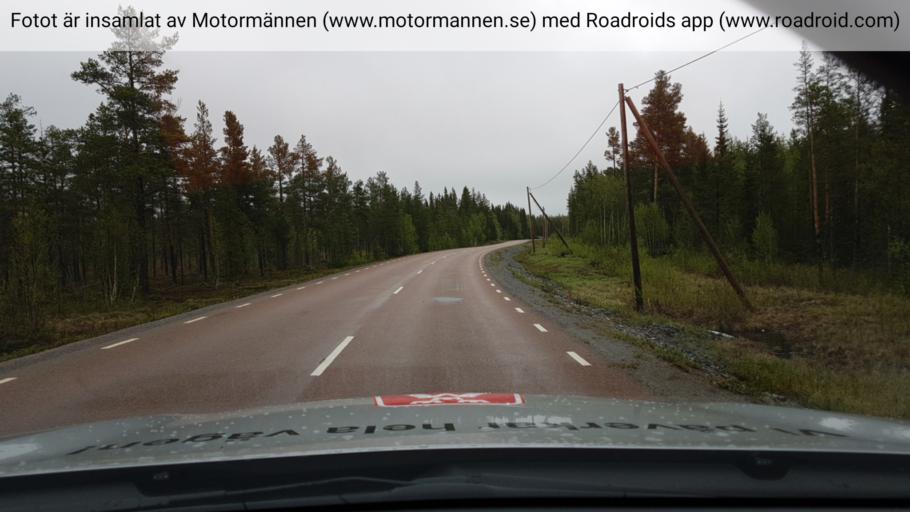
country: SE
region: Jaemtland
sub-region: Krokoms Kommun
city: Valla
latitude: 63.1596
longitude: 13.9762
